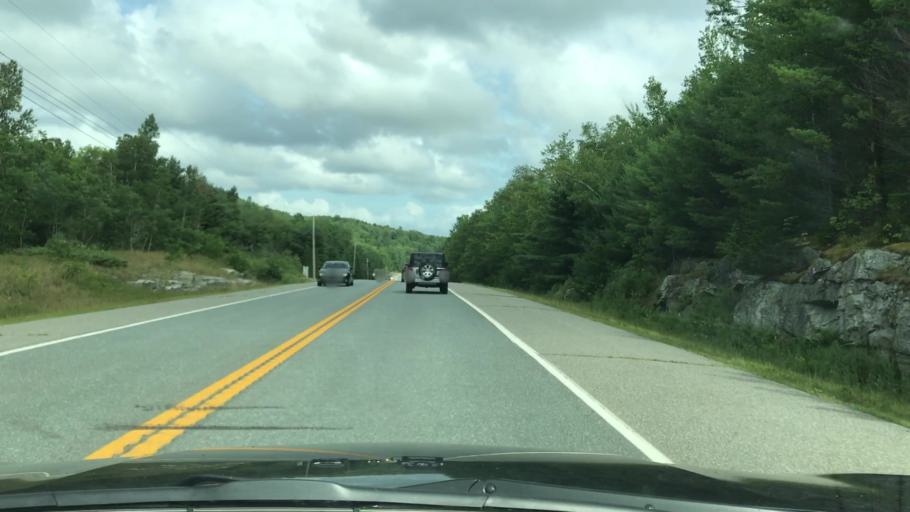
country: US
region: Maine
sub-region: Hancock County
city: Surry
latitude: 44.5642
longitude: -68.5994
